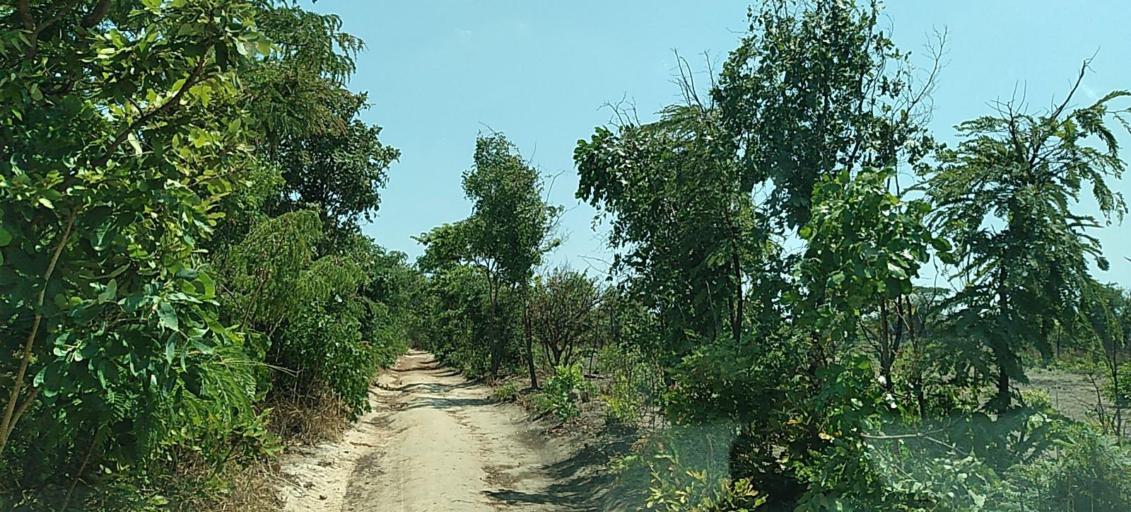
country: ZM
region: Copperbelt
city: Luanshya
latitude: -12.9790
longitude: 28.3301
